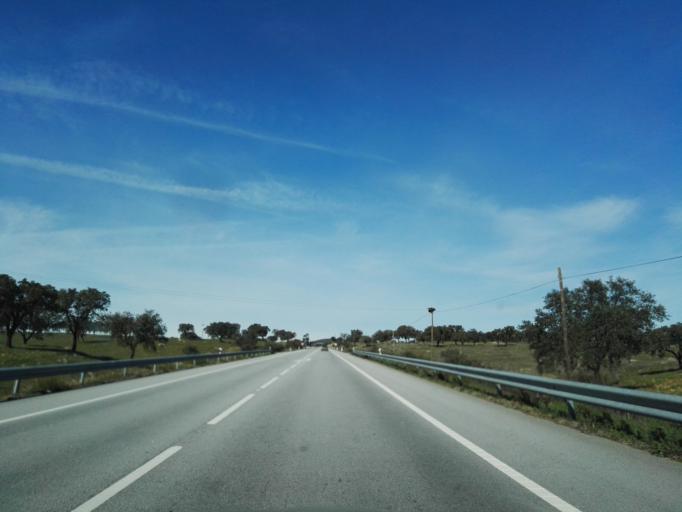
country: PT
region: Portalegre
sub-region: Portalegre
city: Urra
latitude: 39.2004
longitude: -7.3654
